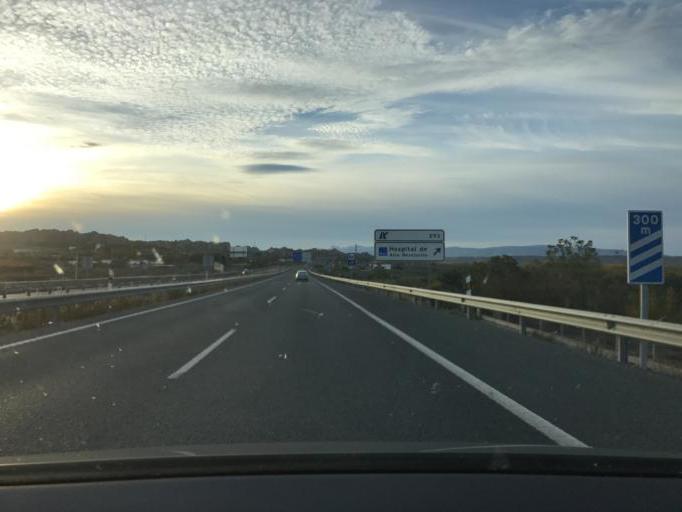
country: ES
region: Andalusia
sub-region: Provincia de Granada
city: Guadix
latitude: 37.3198
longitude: -3.1454
